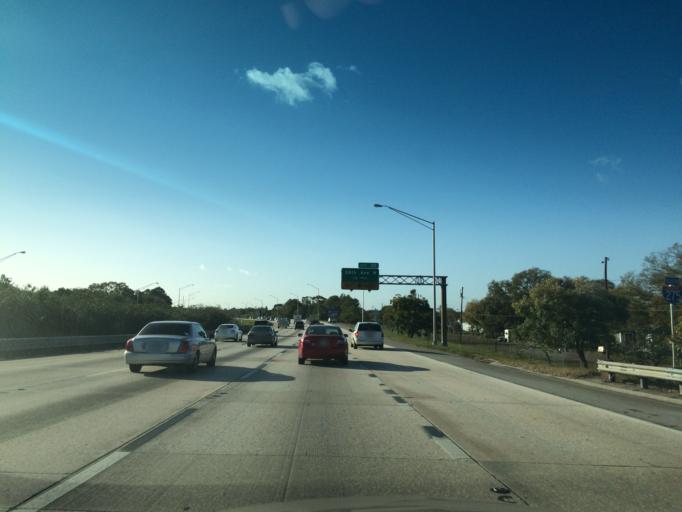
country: US
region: Florida
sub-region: Pinellas County
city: Lealman
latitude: 27.8154
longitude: -82.6649
